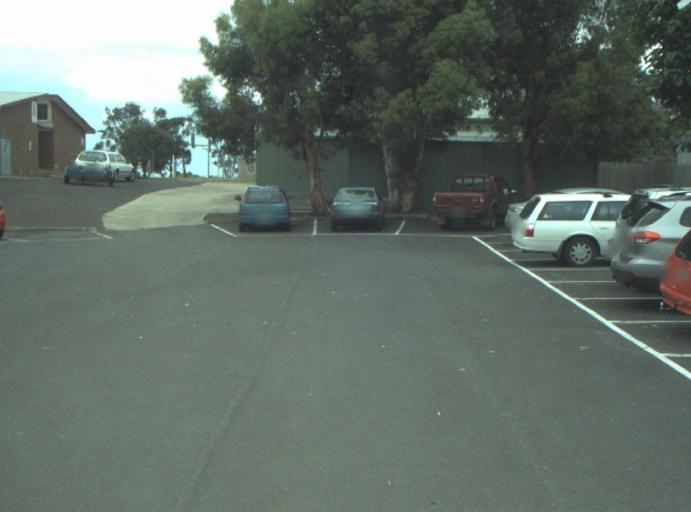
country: AU
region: Victoria
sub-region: Greater Geelong
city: Breakwater
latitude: -38.1871
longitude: 144.3374
